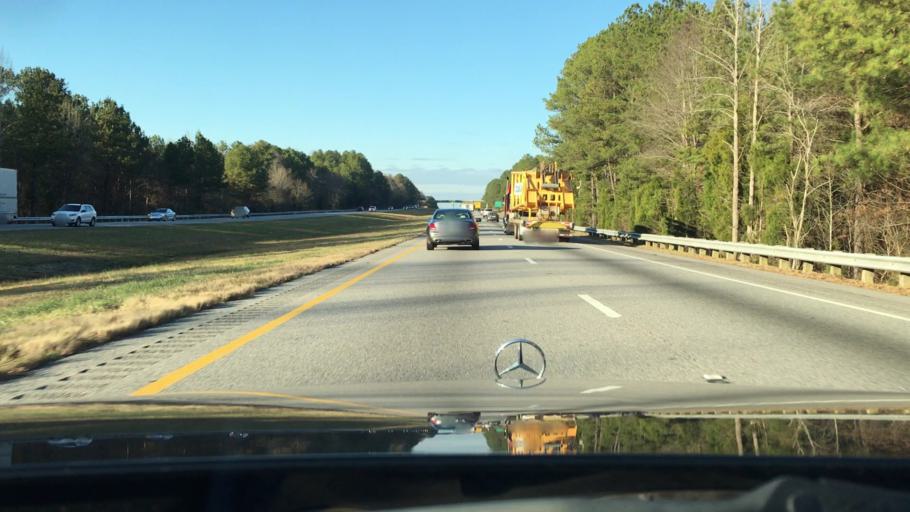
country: US
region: South Carolina
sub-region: Chester County
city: Eureka Mill
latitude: 34.6894
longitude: -81.0294
